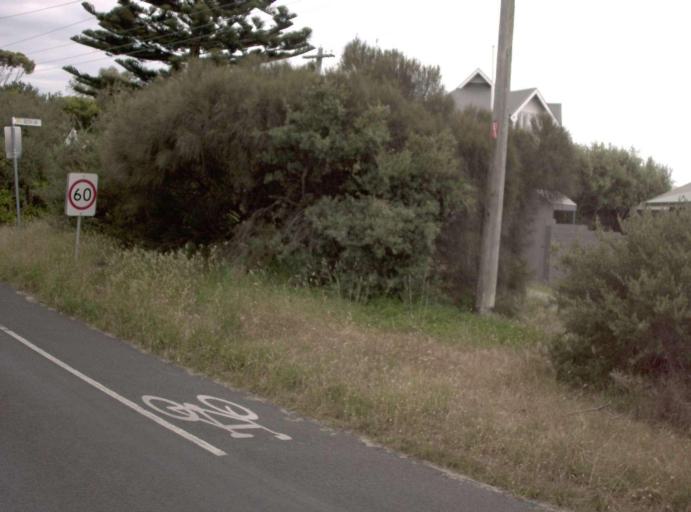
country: AU
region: Victoria
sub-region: Mornington Peninsula
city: Sorrento
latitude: -38.3382
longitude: 144.7413
